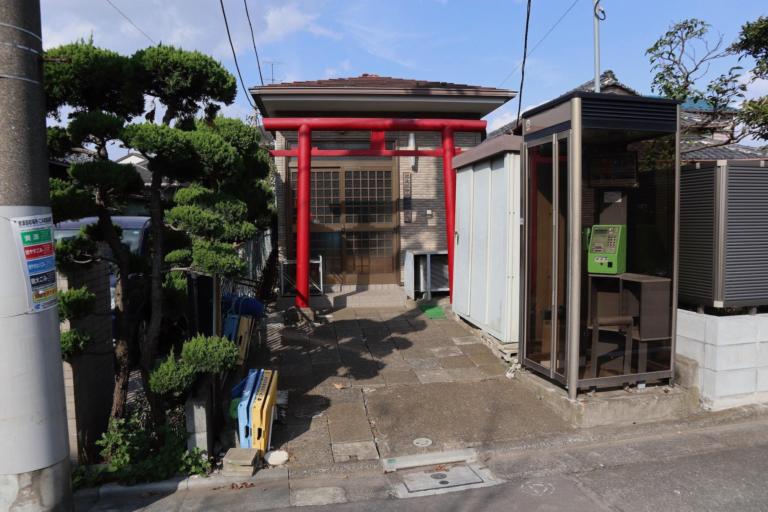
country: JP
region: Tokyo
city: Urayasu
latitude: 35.6753
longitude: 139.8753
